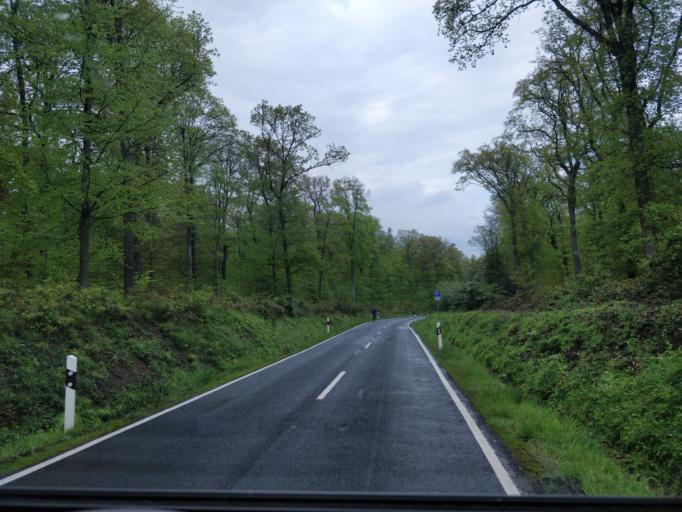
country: DE
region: North Rhine-Westphalia
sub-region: Regierungsbezirk Koln
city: Rheinbach
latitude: 50.5984
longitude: 6.9496
